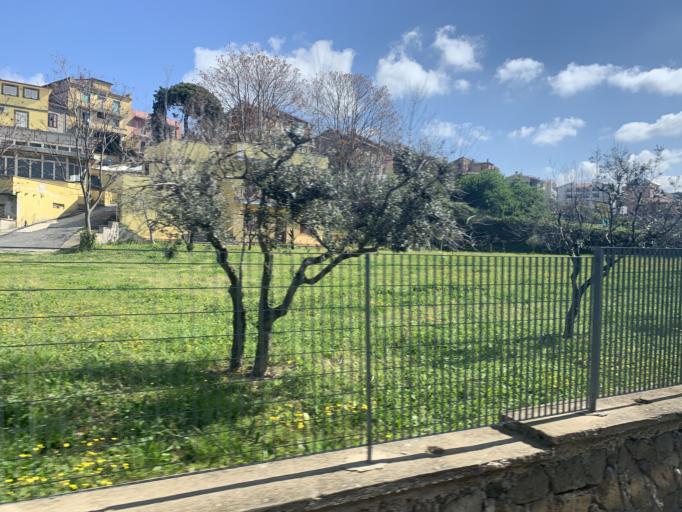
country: IT
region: Latium
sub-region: Citta metropolitana di Roma Capitale
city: Marino
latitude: 41.7708
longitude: 12.6478
